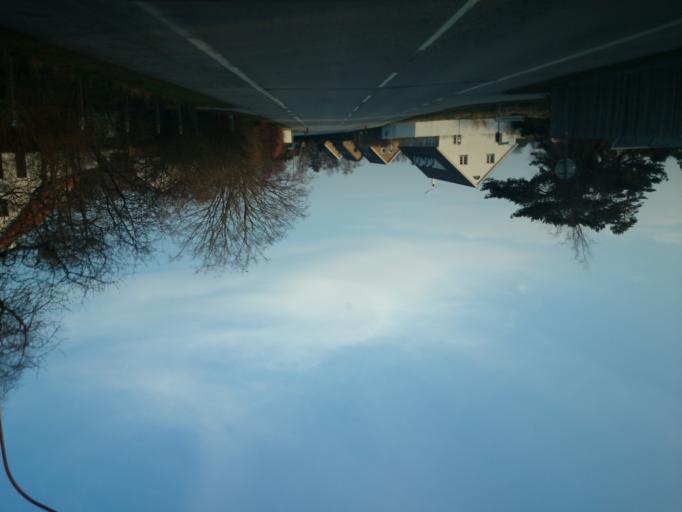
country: SE
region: Skane
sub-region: Vellinge Kommun
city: Skanor med Falsterbo
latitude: 55.4100
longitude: 12.8422
